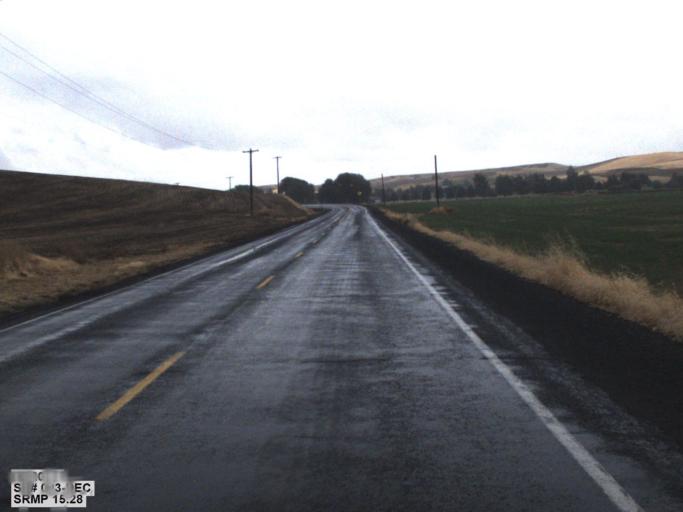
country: US
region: Washington
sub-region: Whitman County
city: Colfax
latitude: 47.0978
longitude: -117.6026
